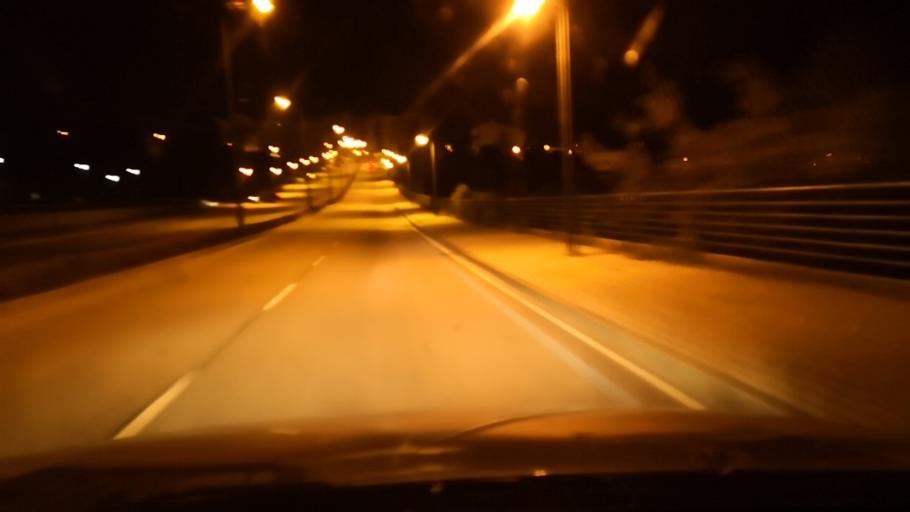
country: PT
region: Castelo Branco
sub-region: Concelho do Fundao
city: Fundao
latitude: 40.1435
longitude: -7.5026
